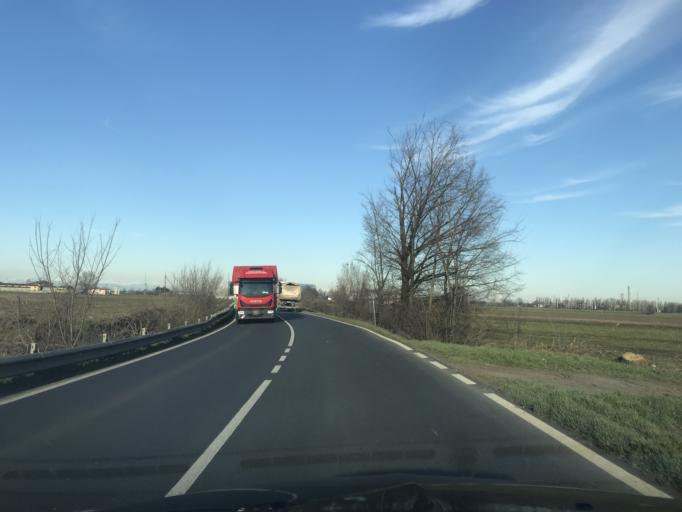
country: IT
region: Lombardy
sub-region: Provincia di Lodi
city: Borgo San Giovanni
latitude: 45.2642
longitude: 9.4371
